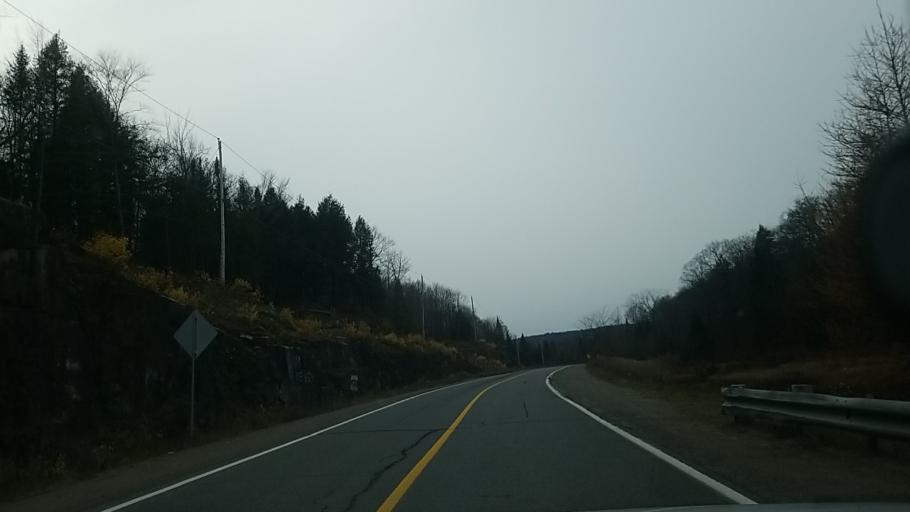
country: CA
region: Quebec
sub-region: Laurentides
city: Saint-Colomban
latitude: 45.7948
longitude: -74.1591
